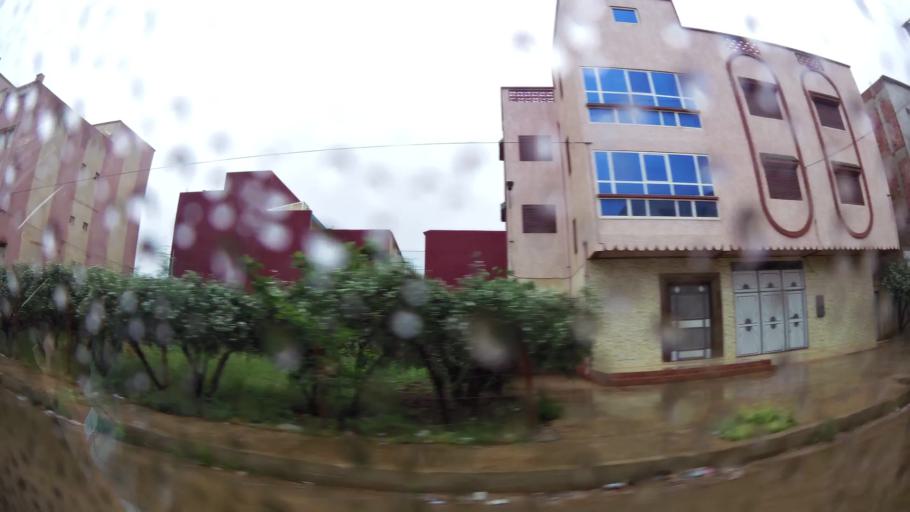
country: MA
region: Oriental
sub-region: Nador
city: Boudinar
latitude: 35.1190
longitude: -3.6439
